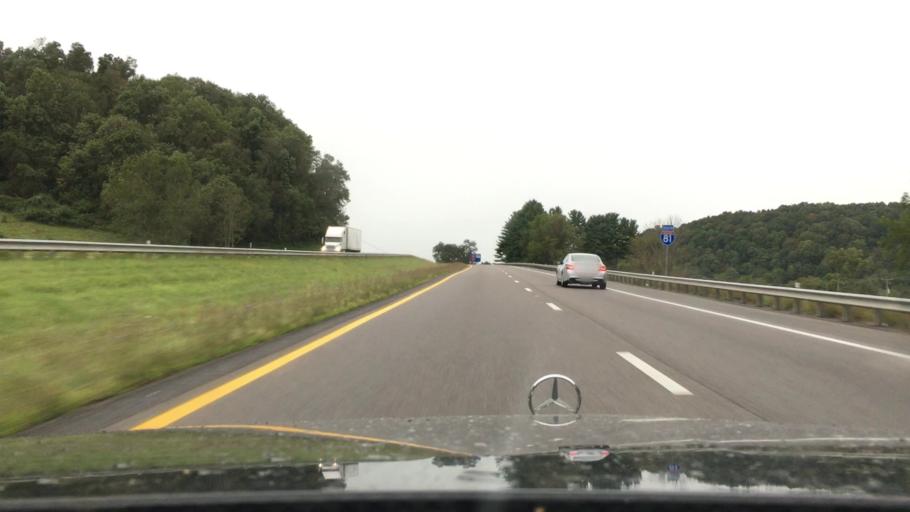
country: US
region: Virginia
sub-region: Smyth County
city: Atkins
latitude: 36.8623
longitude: -81.4442
